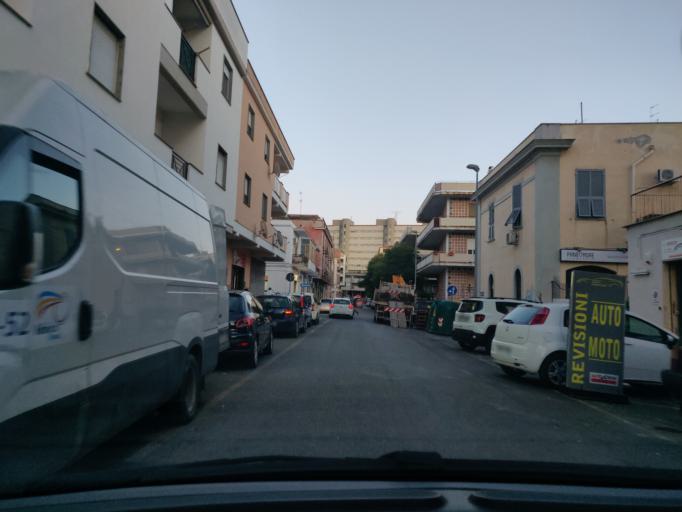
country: IT
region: Latium
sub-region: Citta metropolitana di Roma Capitale
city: Civitavecchia
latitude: 42.0925
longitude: 11.7979
